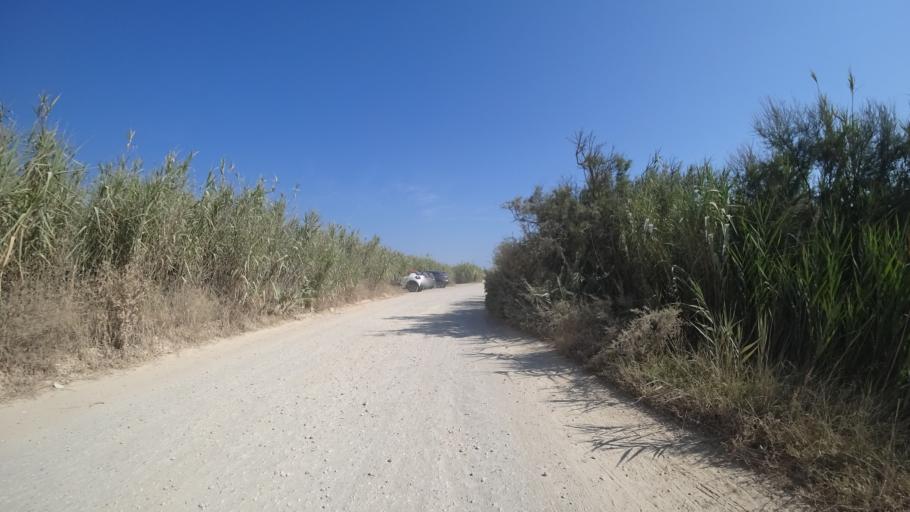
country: FR
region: Languedoc-Roussillon
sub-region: Departement des Pyrenees-Orientales
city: Le Barcares
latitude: 42.7714
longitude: 3.0356
